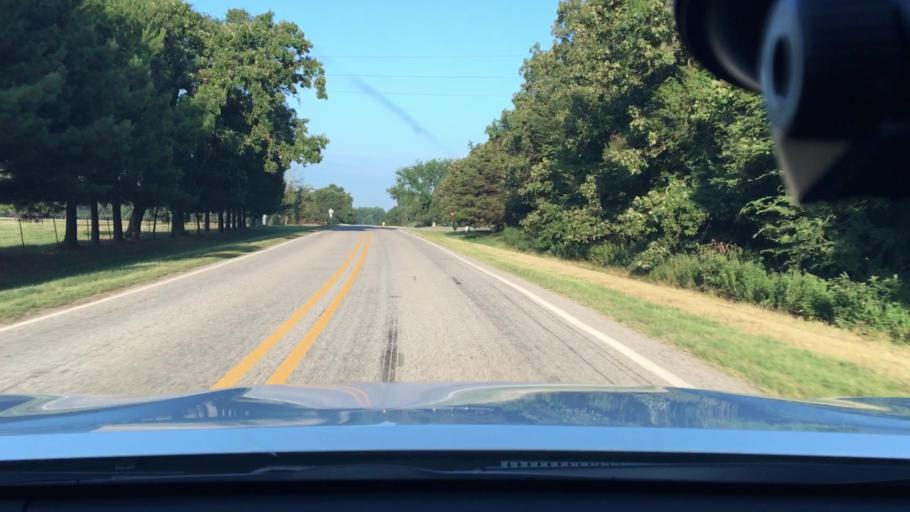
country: US
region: Arkansas
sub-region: Johnson County
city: Coal Hill
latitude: 35.3573
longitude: -93.5607
